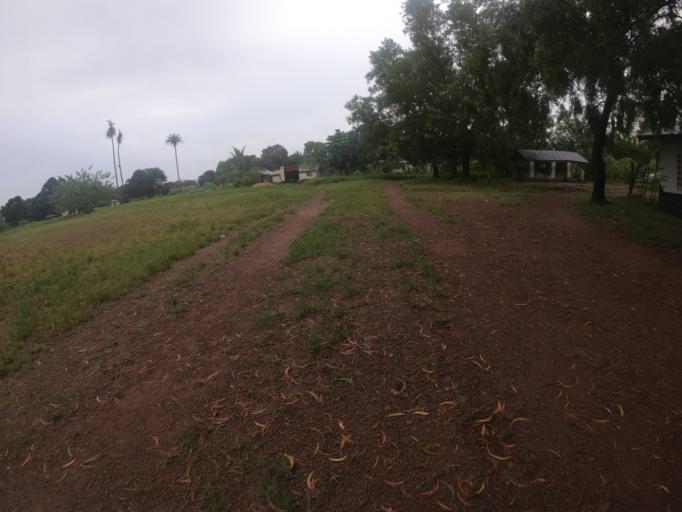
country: SL
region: Southern Province
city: Rotifunk
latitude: 8.4905
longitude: -12.7493
